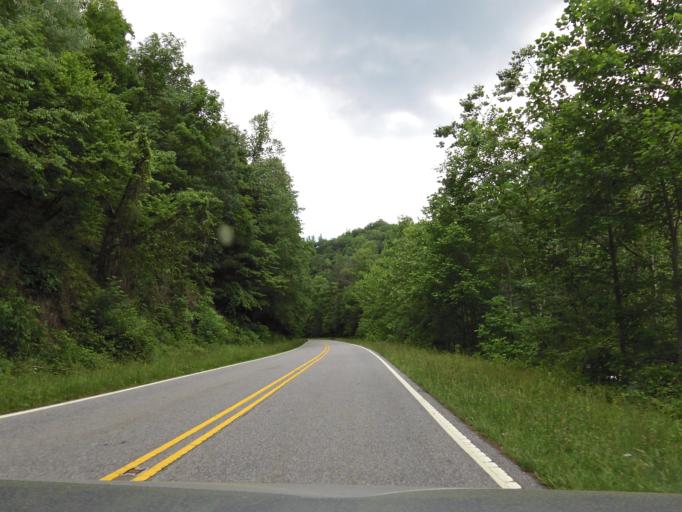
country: US
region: North Carolina
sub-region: Graham County
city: Robbinsville
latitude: 35.4136
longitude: -83.8887
